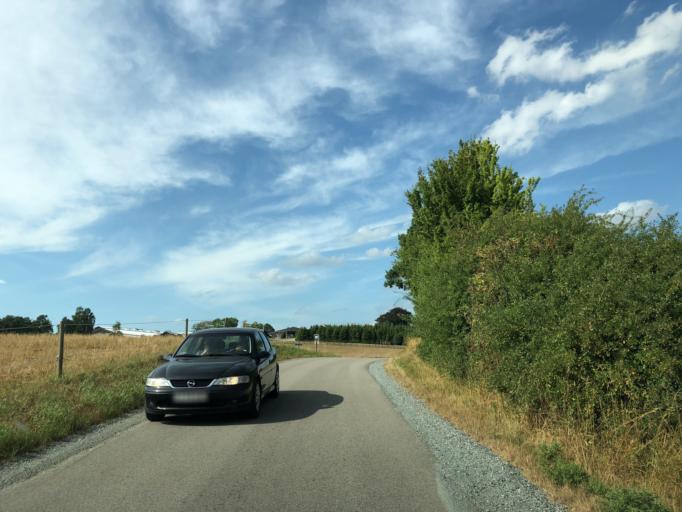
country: DK
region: South Denmark
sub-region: Vejle Kommune
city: Egtved
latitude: 55.6706
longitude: 9.3027
